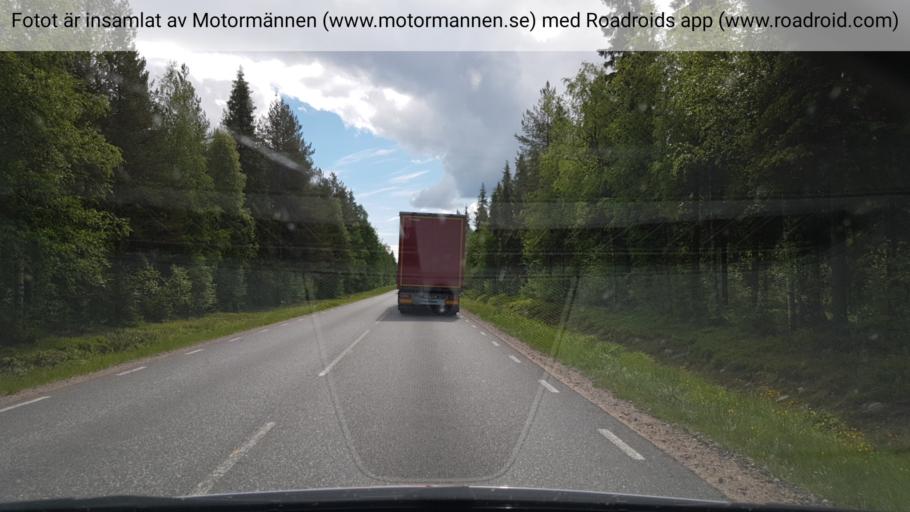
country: FI
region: Lapland
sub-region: Torniolaakso
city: Ylitornio
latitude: 66.2526
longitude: 23.6641
